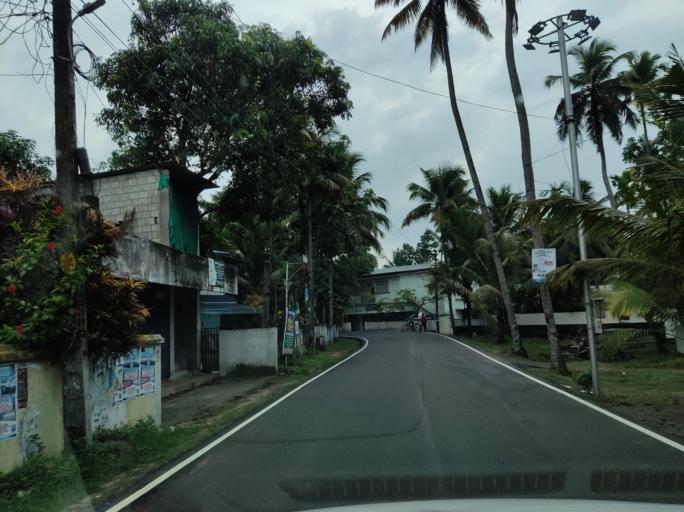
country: IN
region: Kerala
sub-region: Alappuzha
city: Kayankulam
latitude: 9.2673
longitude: 76.4047
